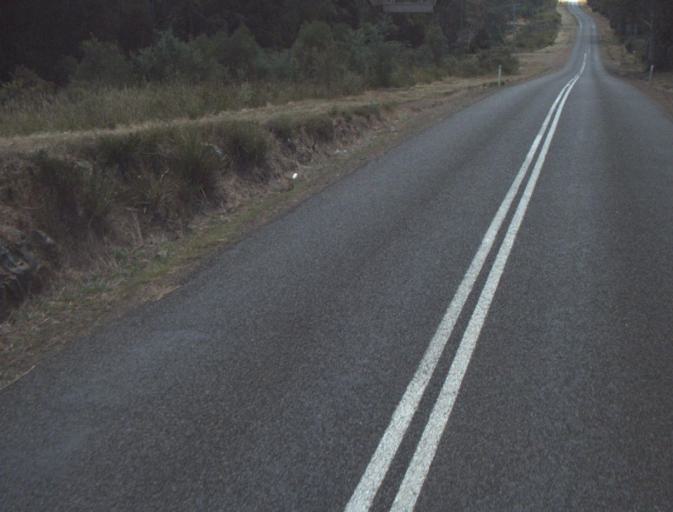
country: AU
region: Tasmania
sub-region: Launceston
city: Mayfield
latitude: -41.3146
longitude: 147.1352
